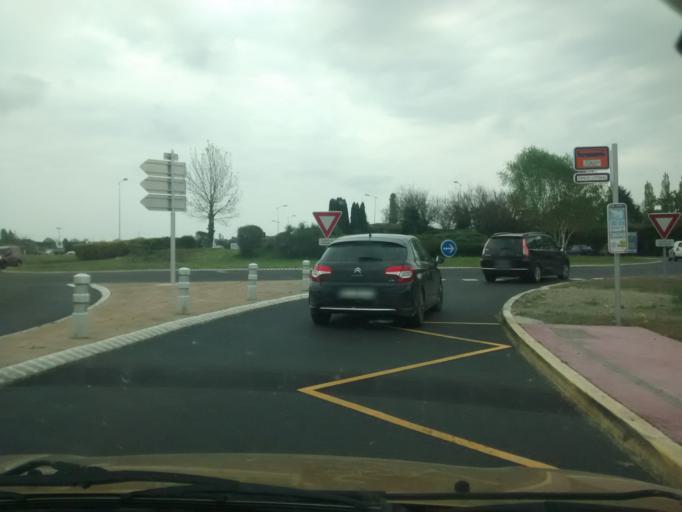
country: FR
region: Brittany
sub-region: Departement du Morbihan
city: Muzillac
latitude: 47.5589
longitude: -2.5073
